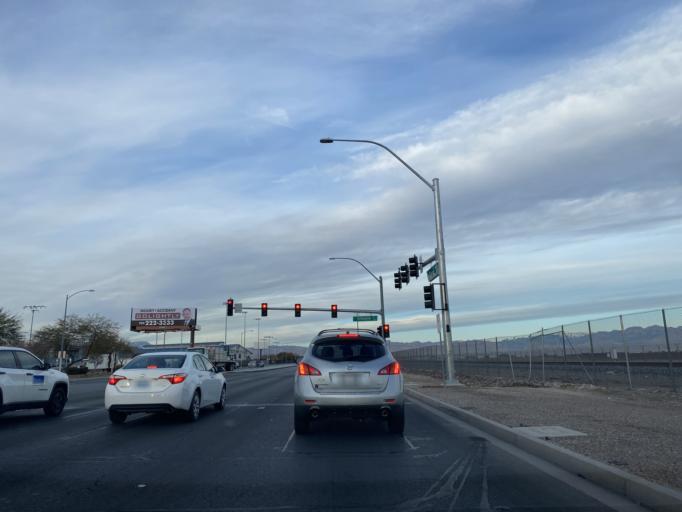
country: US
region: Nevada
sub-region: Clark County
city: Paradise
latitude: 36.0968
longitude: -115.1649
